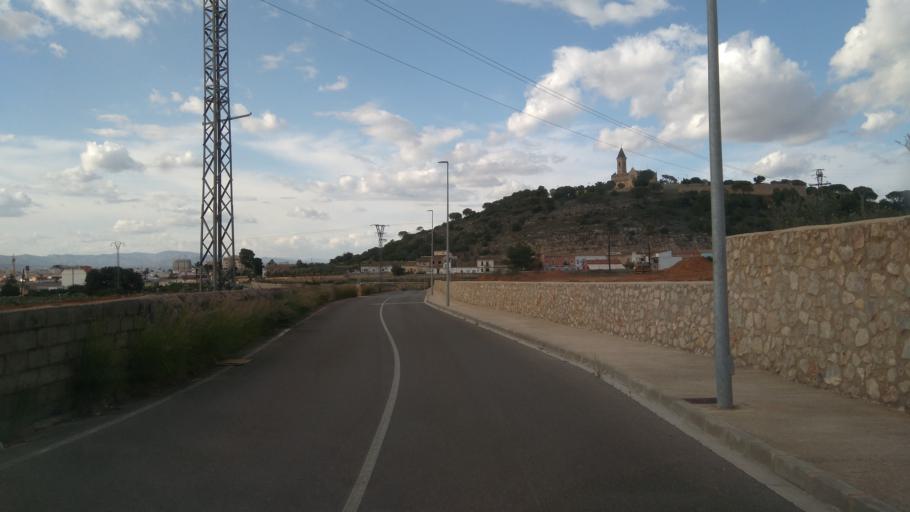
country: ES
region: Valencia
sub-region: Provincia de Valencia
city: Alzira
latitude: 39.1485
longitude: -0.4162
